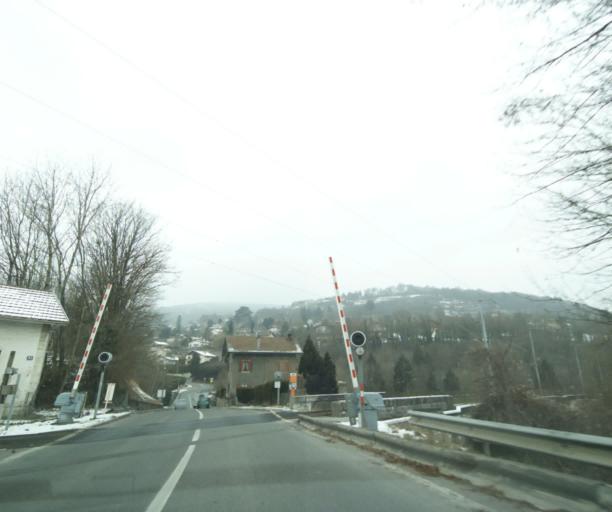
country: FR
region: Rhone-Alpes
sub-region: Departement de la Haute-Savoie
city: Vetraz-Monthoux
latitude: 46.1618
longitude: 6.2417
